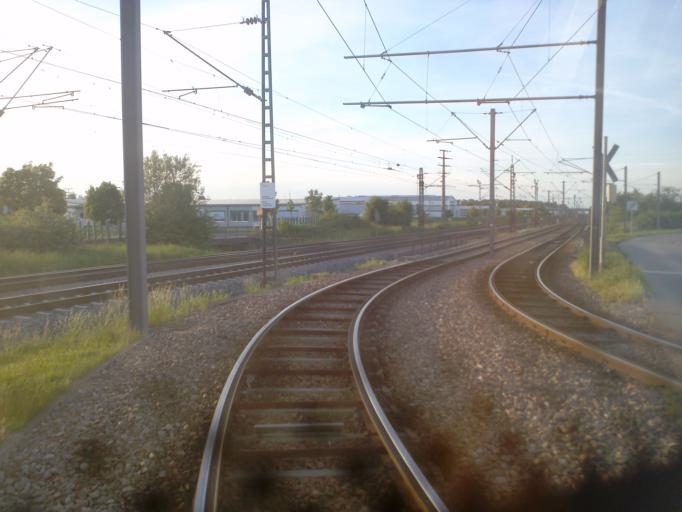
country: DE
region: Baden-Wuerttemberg
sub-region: Karlsruhe Region
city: Weingarten
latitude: 49.0734
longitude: 8.4669
